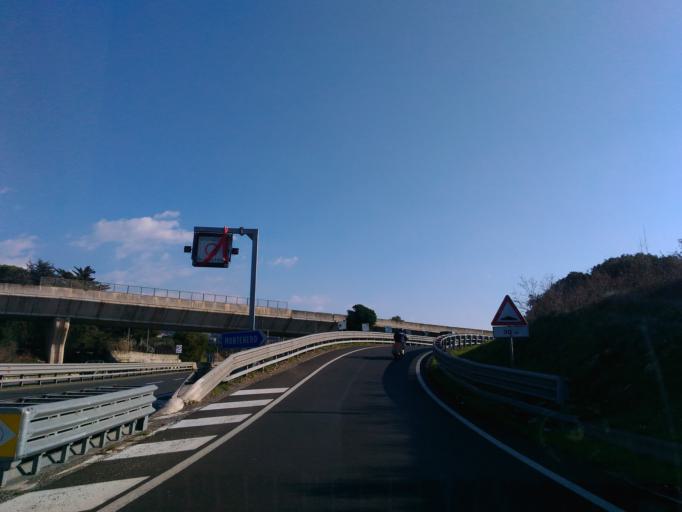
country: IT
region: Tuscany
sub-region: Provincia di Livorno
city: Livorno
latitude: 43.5127
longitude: 10.3332
